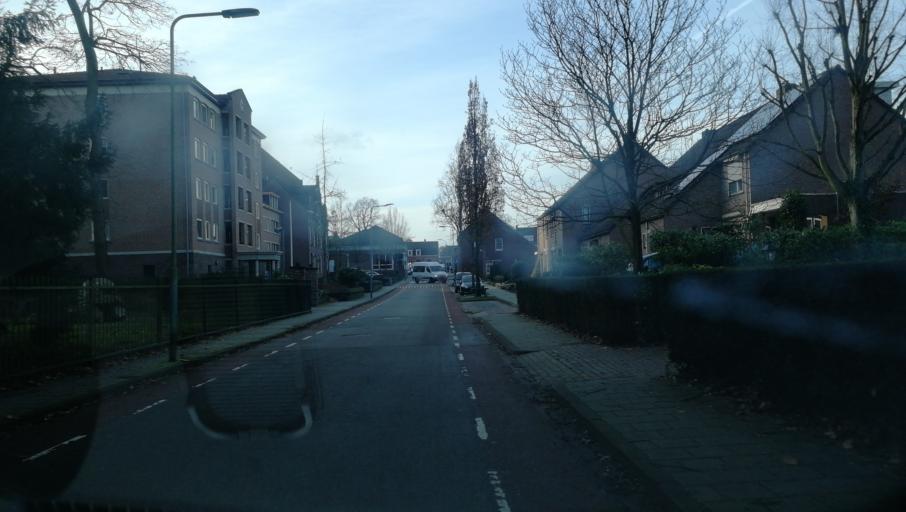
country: NL
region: Limburg
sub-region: Gemeente Venlo
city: Tegelen
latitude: 51.3314
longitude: 6.0995
